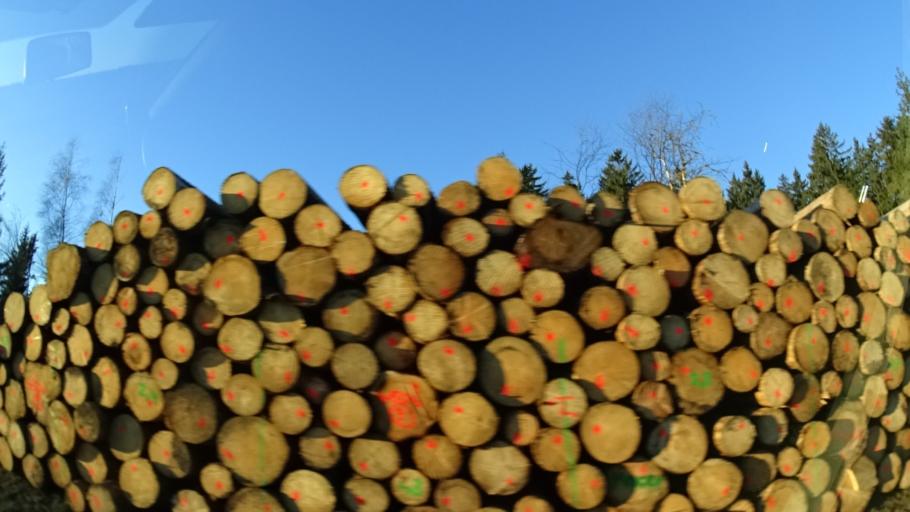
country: DE
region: Thuringia
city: Grafenthal
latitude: 50.5451
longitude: 11.2773
